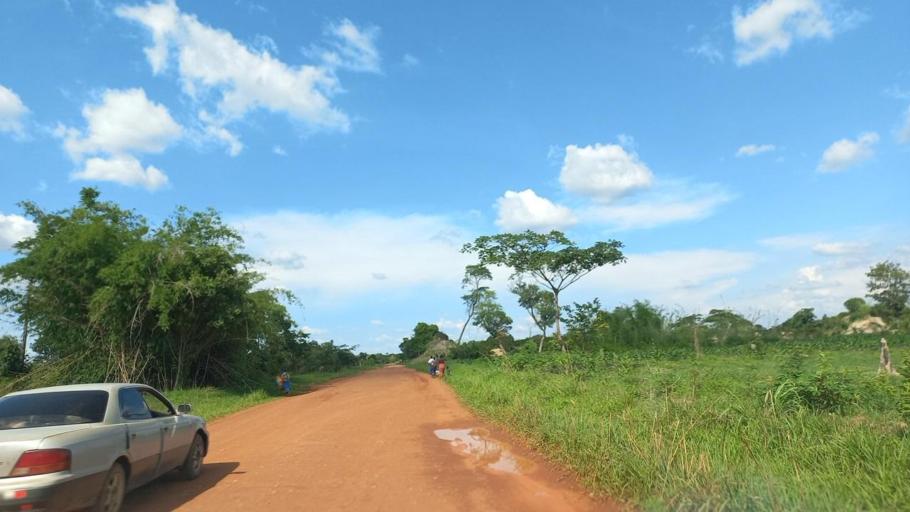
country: ZM
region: Copperbelt
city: Kitwe
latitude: -12.8572
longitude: 28.3855
